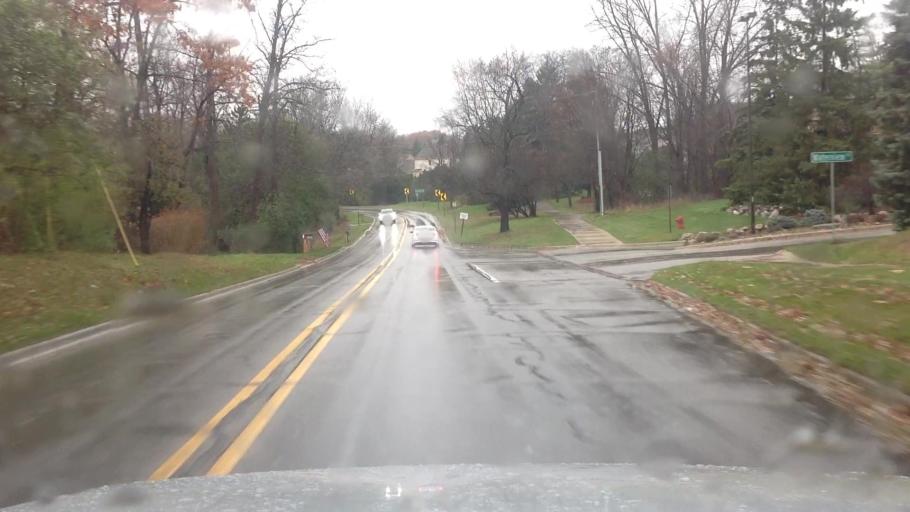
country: US
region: Michigan
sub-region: Oakland County
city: West Bloomfield Township
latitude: 42.5579
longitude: -83.4072
